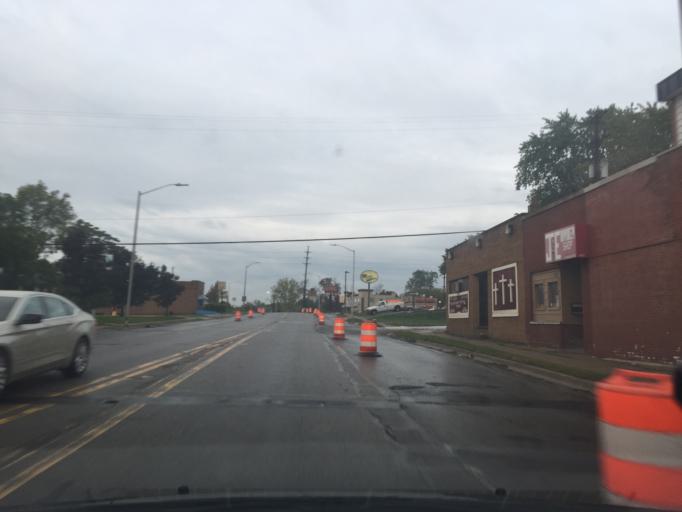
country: US
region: Michigan
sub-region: Oakland County
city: Pontiac
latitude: 42.6493
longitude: -83.2858
